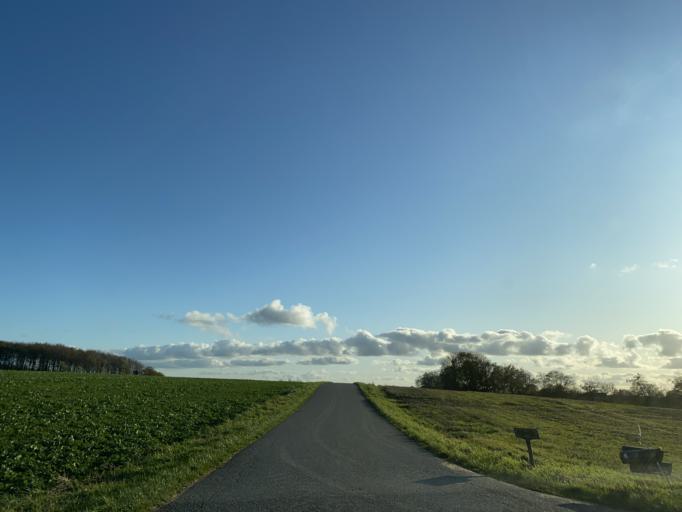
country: DK
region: Central Jutland
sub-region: Viborg Kommune
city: Bjerringbro
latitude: 56.3435
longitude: 9.7146
